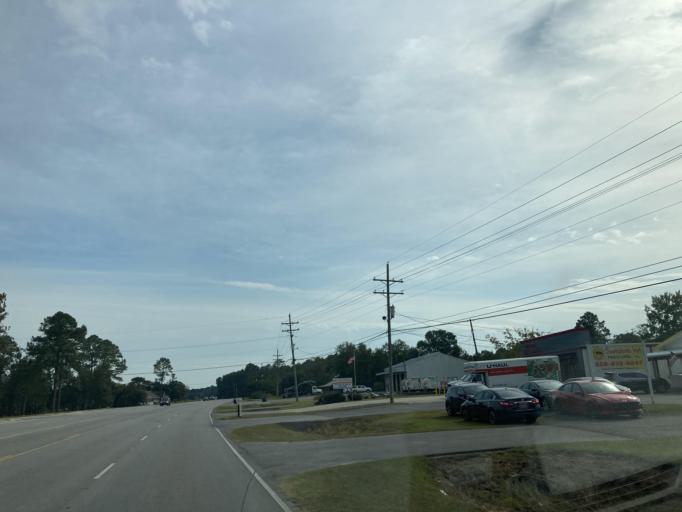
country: US
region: Mississippi
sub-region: Jackson County
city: Saint Martin
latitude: 30.4767
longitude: -88.8500
